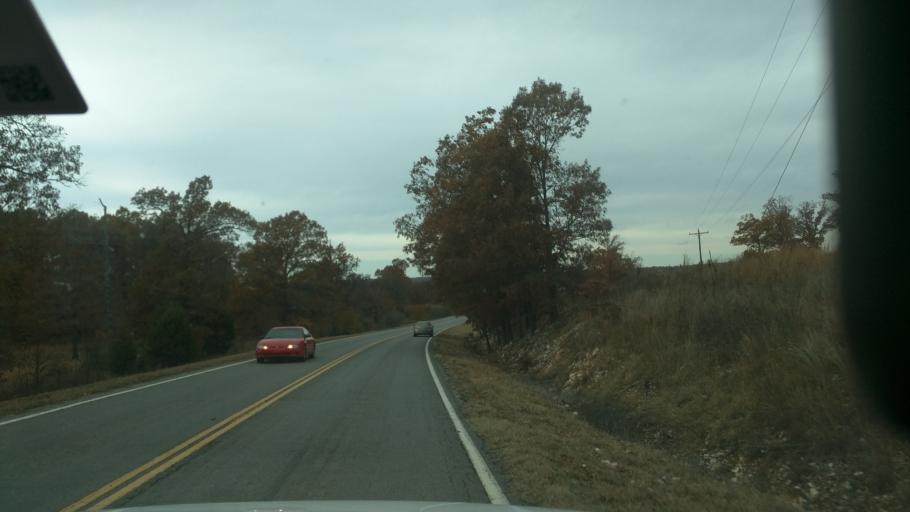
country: US
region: Oklahoma
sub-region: Cherokee County
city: Park Hill
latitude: 35.9034
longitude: -94.8239
